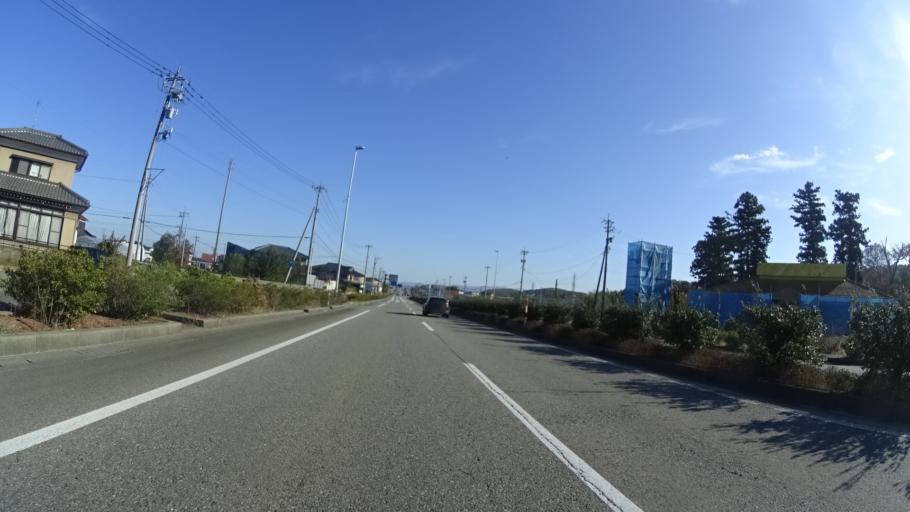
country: JP
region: Ishikawa
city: Komatsu
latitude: 36.3205
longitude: 136.4004
